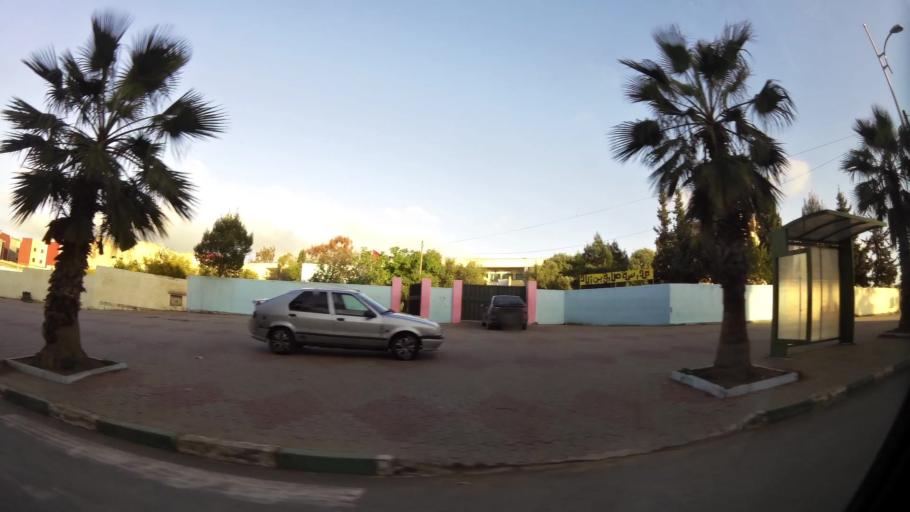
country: MA
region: Chaouia-Ouardigha
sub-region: Settat Province
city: Settat
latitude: 32.9952
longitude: -7.6056
